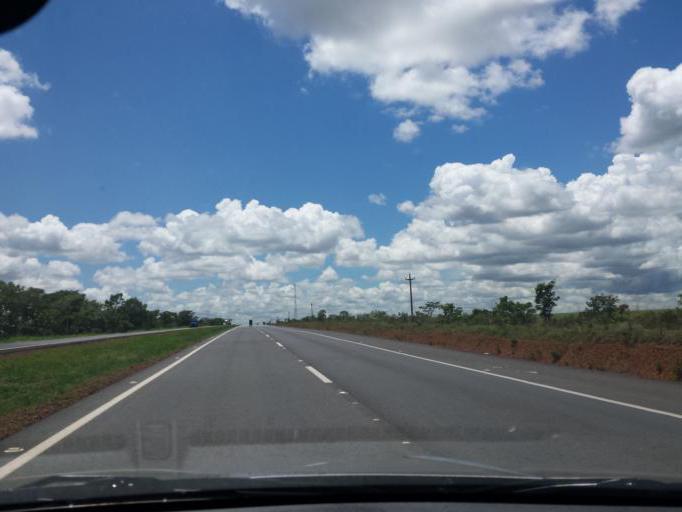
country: BR
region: Goias
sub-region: Cristalina
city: Cristalina
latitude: -16.6707
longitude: -47.7125
